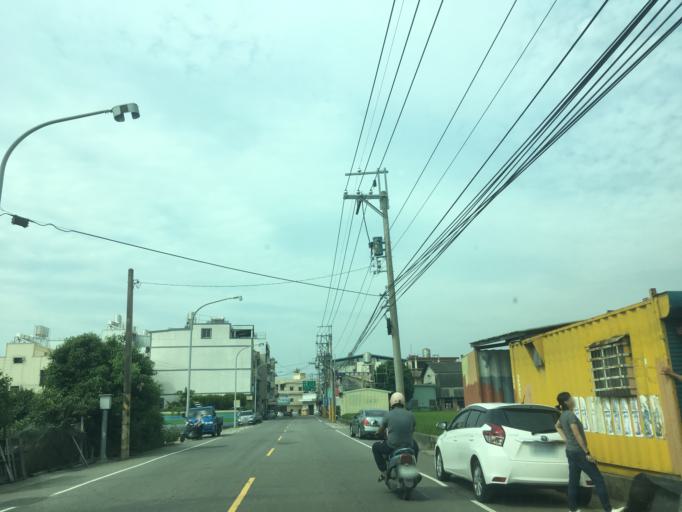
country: TW
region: Taiwan
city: Zhongxing New Village
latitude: 24.0479
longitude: 120.6749
